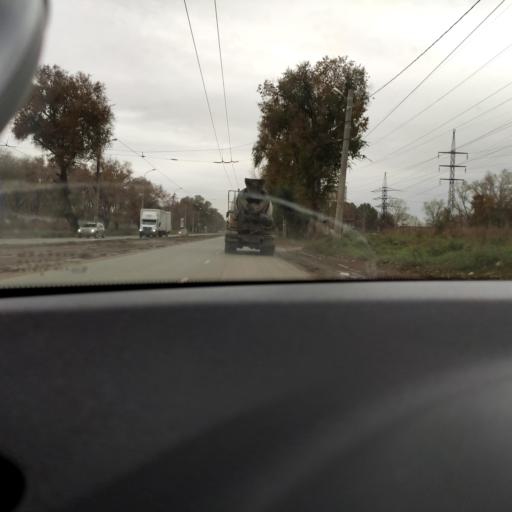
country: RU
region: Samara
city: Smyshlyayevka
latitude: 53.1975
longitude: 50.2886
